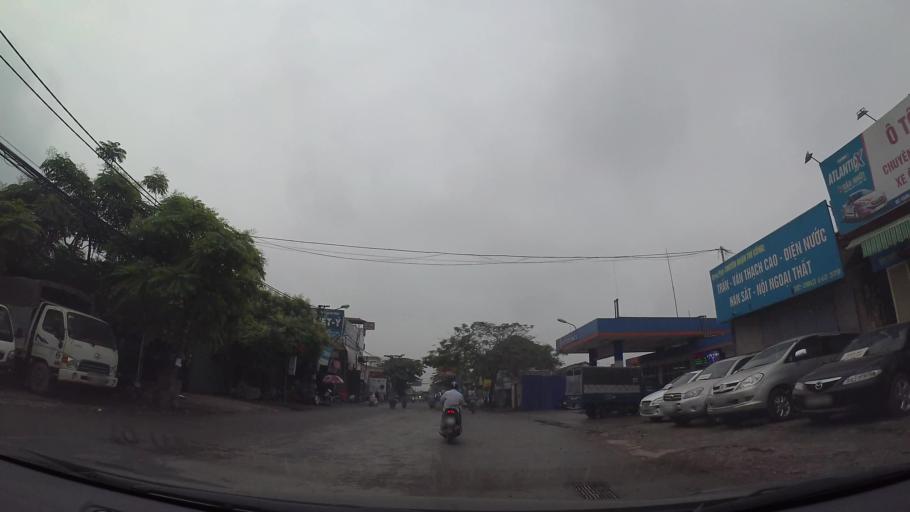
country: VN
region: Ha Noi
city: Van Dien
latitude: 20.9745
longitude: 105.8660
